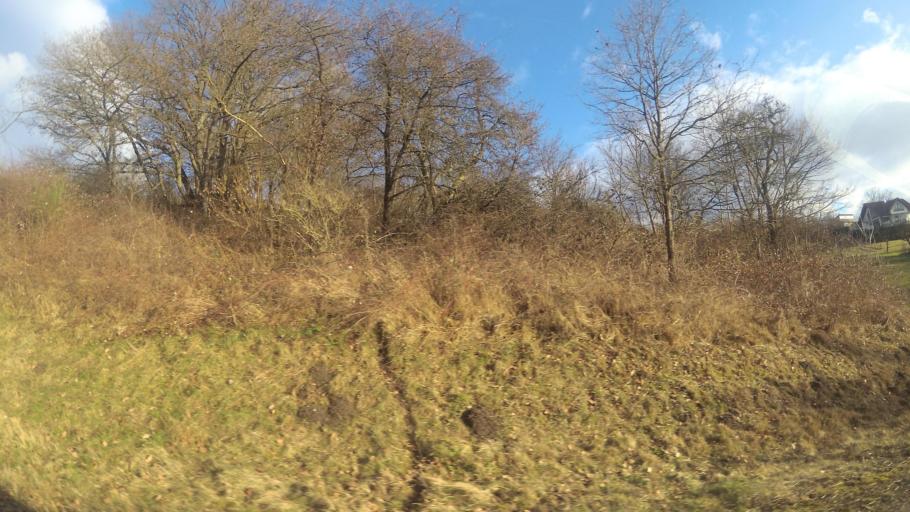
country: DE
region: Rheinland-Pfalz
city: Blaubach
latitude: 49.5593
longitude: 7.3990
